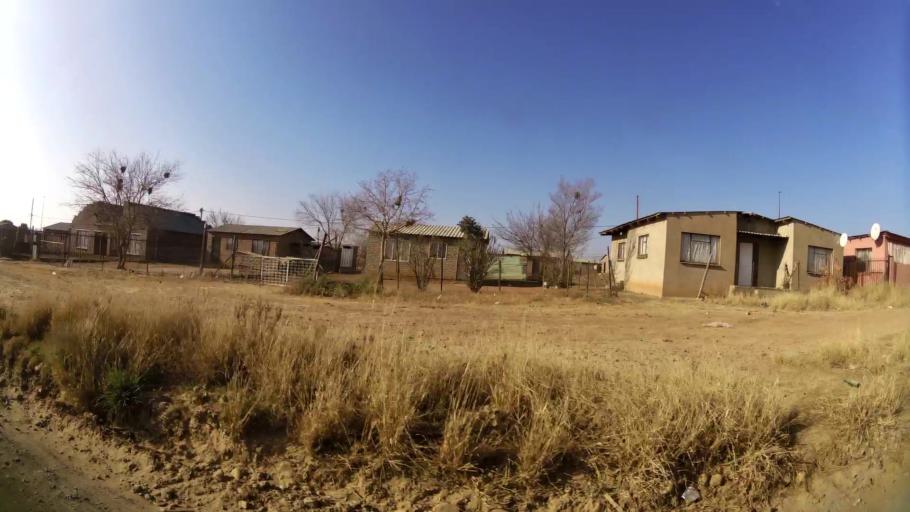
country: ZA
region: Orange Free State
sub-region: Mangaung Metropolitan Municipality
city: Bloemfontein
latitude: -29.1999
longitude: 26.2576
